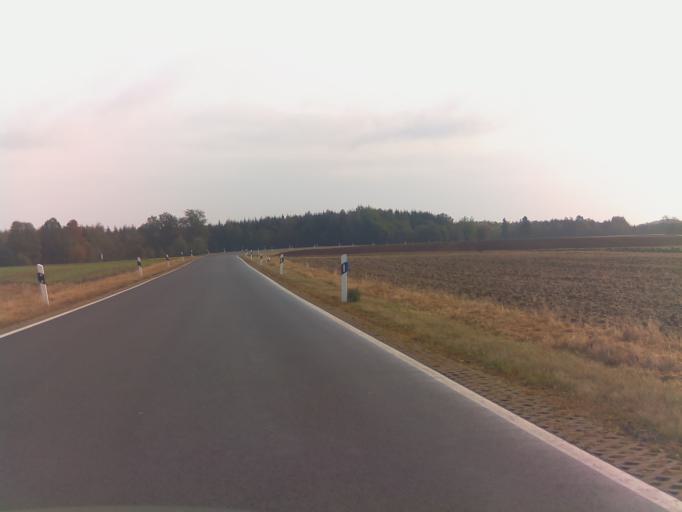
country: DE
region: Hesse
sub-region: Regierungsbezirk Giessen
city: Freiensteinau
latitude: 50.4709
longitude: 9.4134
